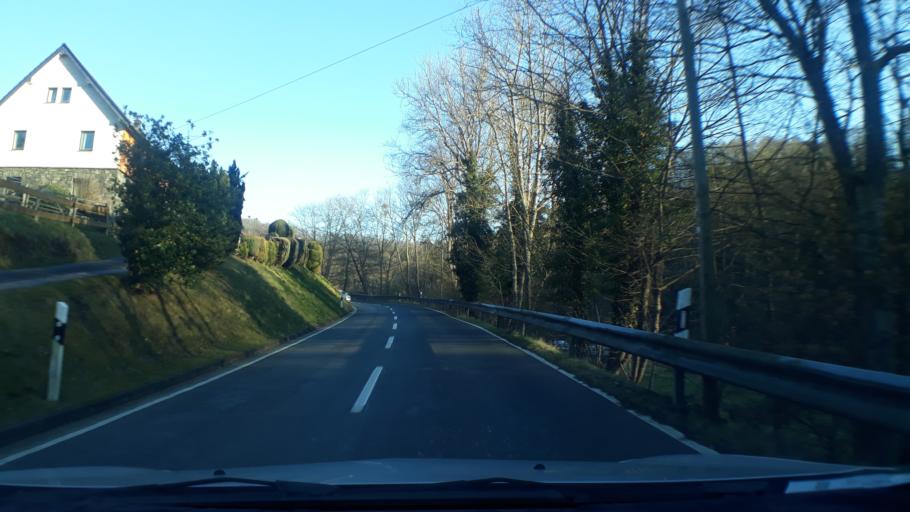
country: DE
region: North Rhine-Westphalia
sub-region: Regierungsbezirk Koln
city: Simmerath
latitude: 50.5835
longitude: 6.3590
